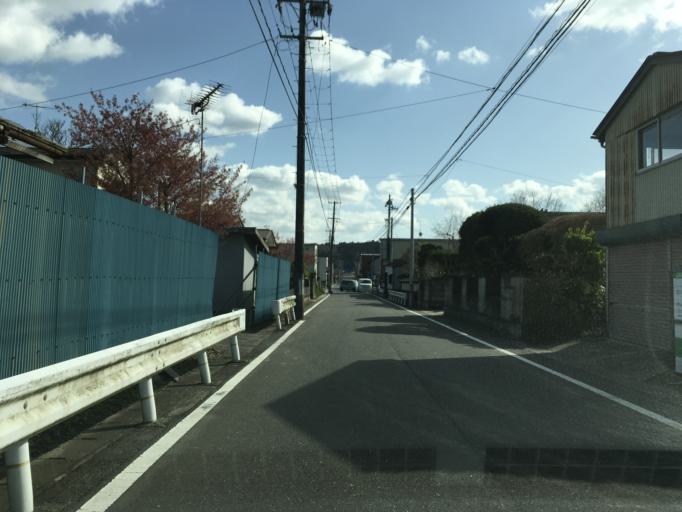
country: JP
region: Miyagi
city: Wakuya
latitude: 38.6577
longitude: 141.2852
